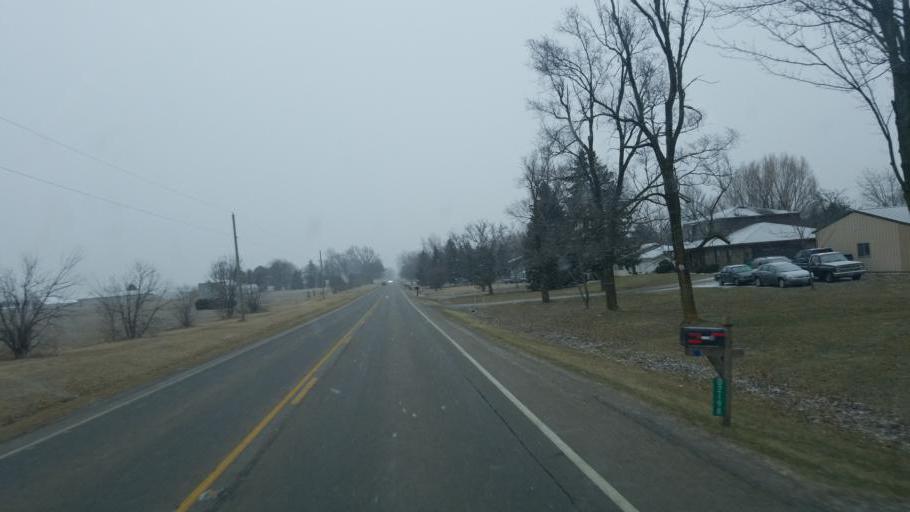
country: US
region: Ohio
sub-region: Defiance County
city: Hicksville
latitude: 41.3077
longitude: -84.7826
